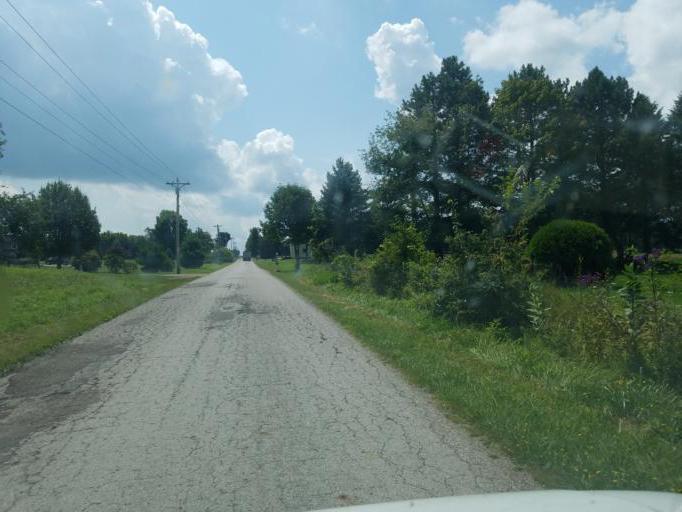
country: US
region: Ohio
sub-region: Knox County
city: Centerburg
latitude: 40.3911
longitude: -82.6529
